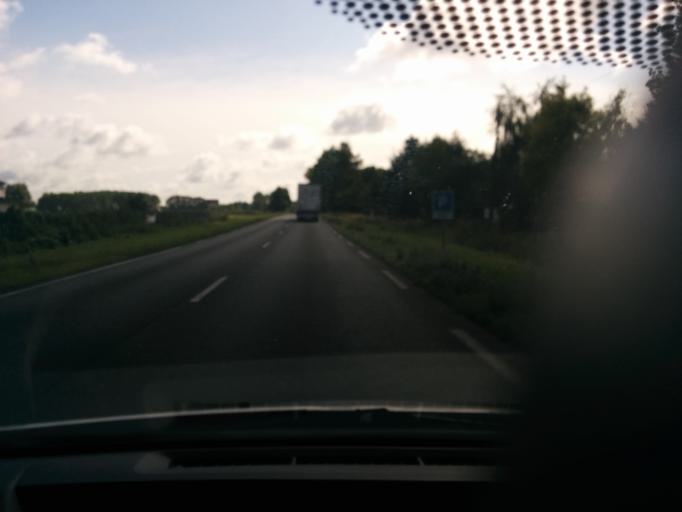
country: FR
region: Pays de la Loire
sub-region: Departement de Maine-et-Loire
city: Andard
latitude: 47.4650
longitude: -0.3972
